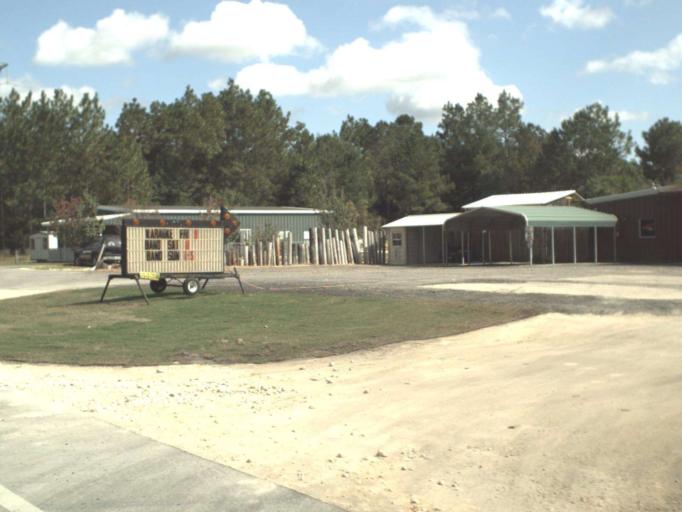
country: US
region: Florida
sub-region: Walton County
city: DeFuniak Springs
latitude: 30.7543
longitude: -86.1135
